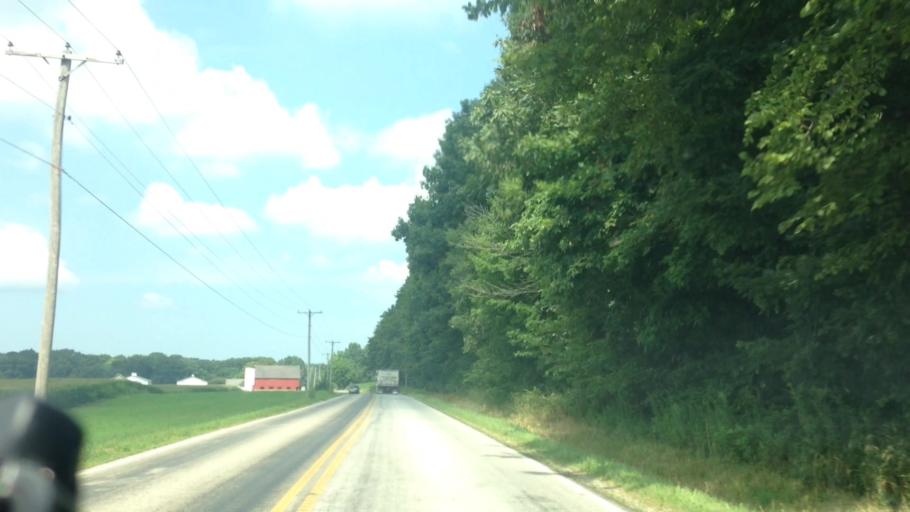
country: US
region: Ohio
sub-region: Wayne County
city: Dalton
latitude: 40.8703
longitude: -81.6967
